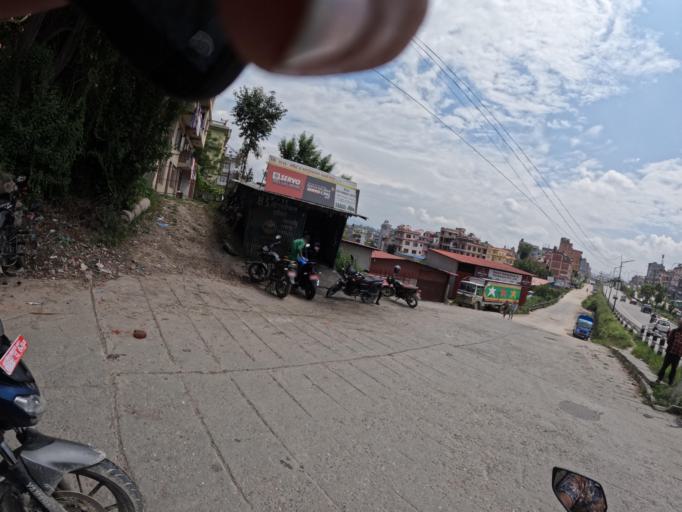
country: NP
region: Central Region
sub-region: Bagmati Zone
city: Patan
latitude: 27.6752
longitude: 85.3610
